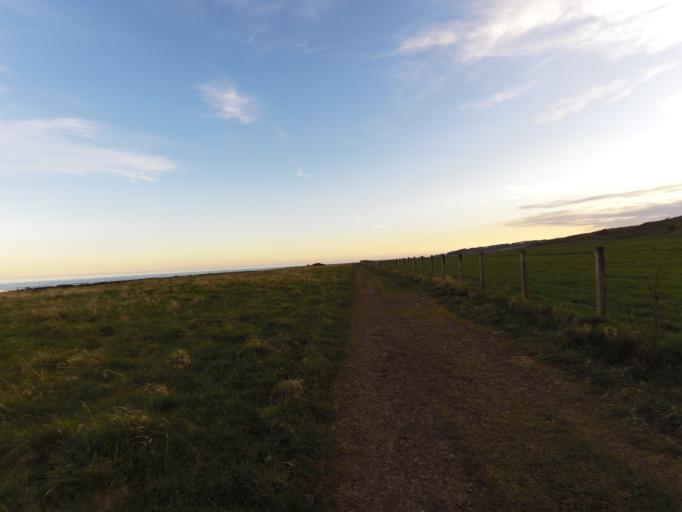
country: GB
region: Scotland
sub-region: Aberdeenshire
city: Inverbervie
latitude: 56.8209
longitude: -2.2952
